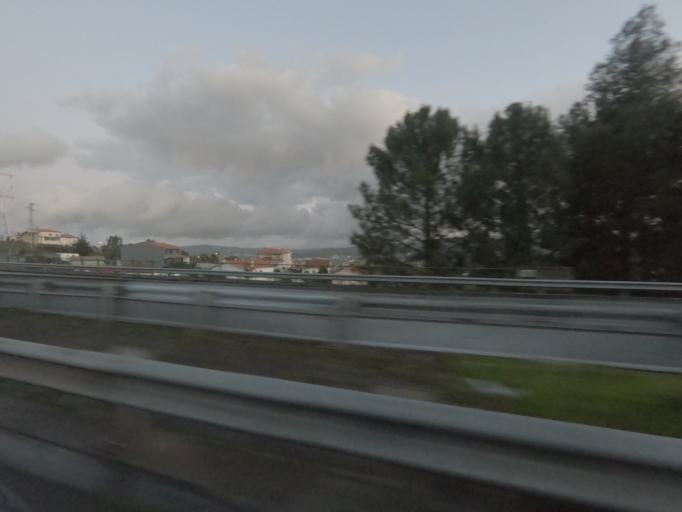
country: PT
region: Porto
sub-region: Paredes
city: Baltar
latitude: 41.1827
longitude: -8.3751
